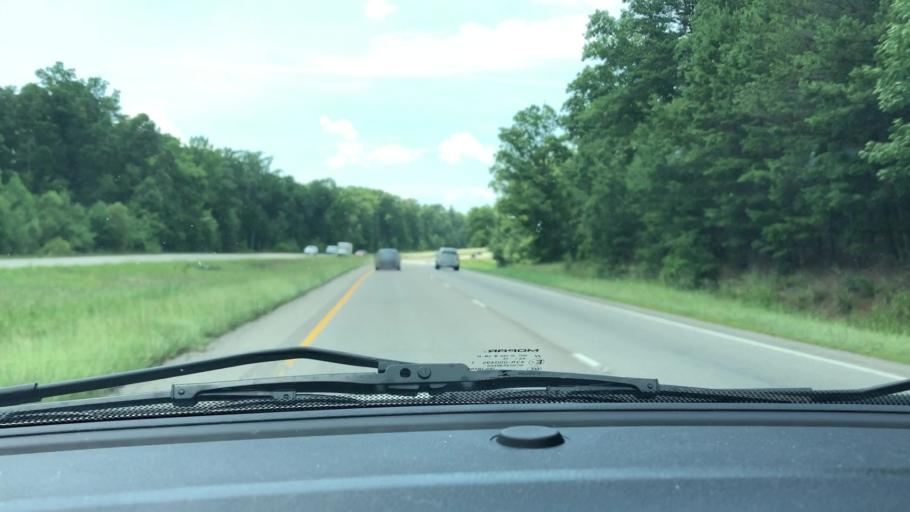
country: US
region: North Carolina
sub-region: Chatham County
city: Farmville
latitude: 35.5709
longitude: -79.3048
